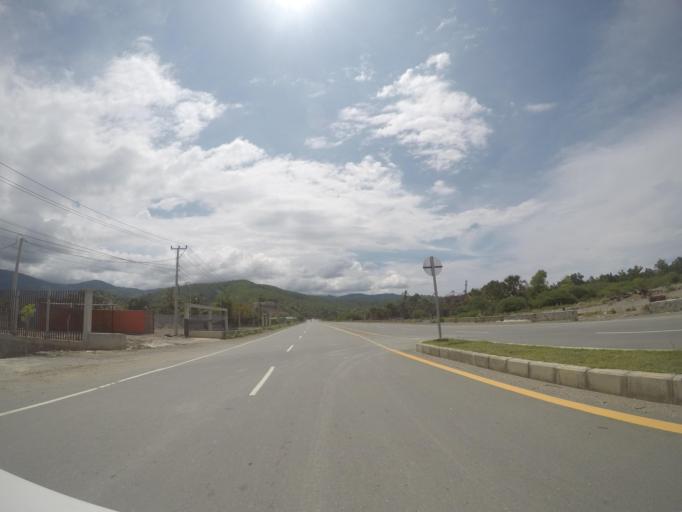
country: TL
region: Dili
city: Dili
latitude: -8.5704
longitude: 125.4873
